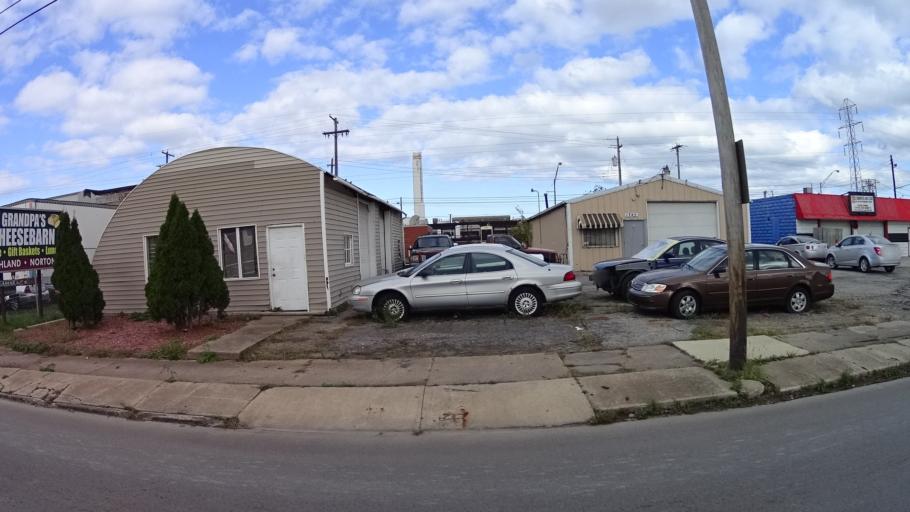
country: US
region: Ohio
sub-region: Lorain County
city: Lorain
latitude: 41.4455
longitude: -82.1393
